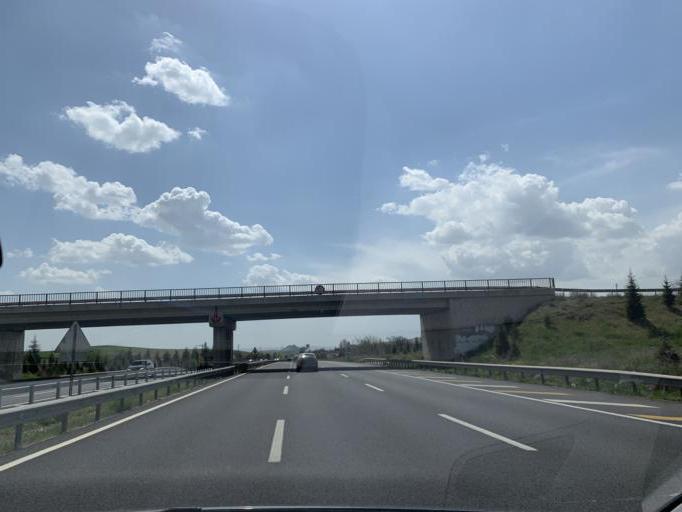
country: TR
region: Ankara
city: Etimesgut
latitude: 39.8006
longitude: 32.5399
